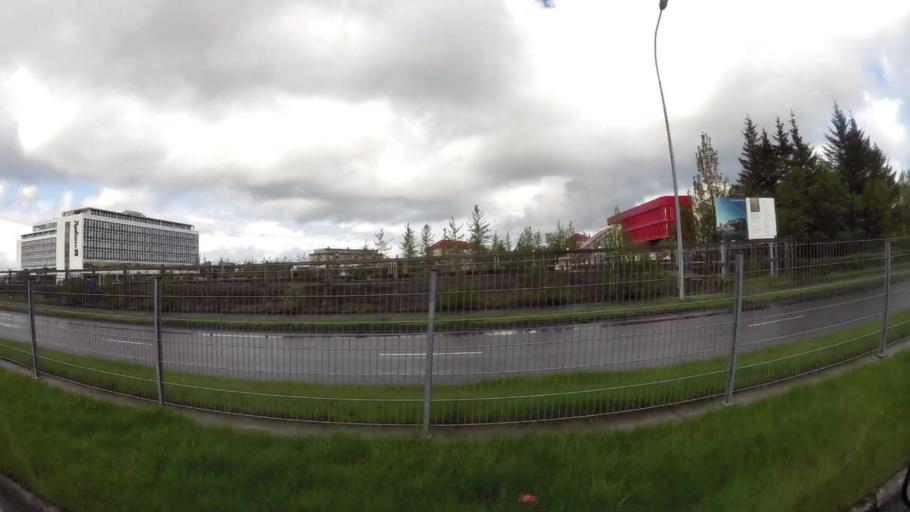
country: IS
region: Capital Region
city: Kopavogur
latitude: 64.1419
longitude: -21.9492
